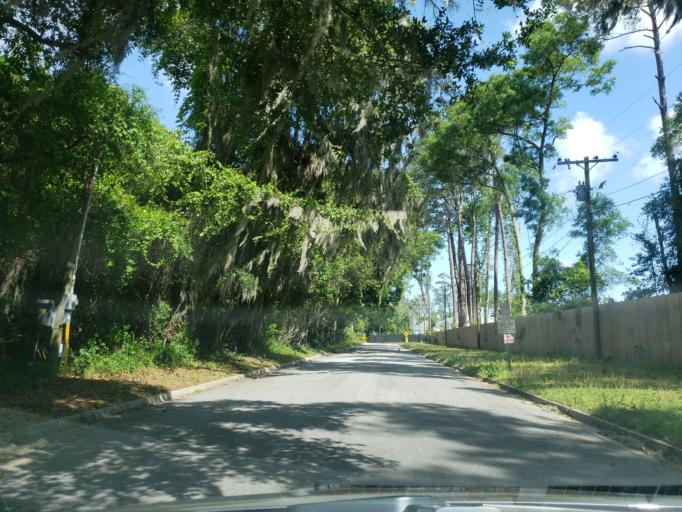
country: US
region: Georgia
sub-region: Chatham County
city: Thunderbolt
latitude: 32.0184
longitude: -81.0635
